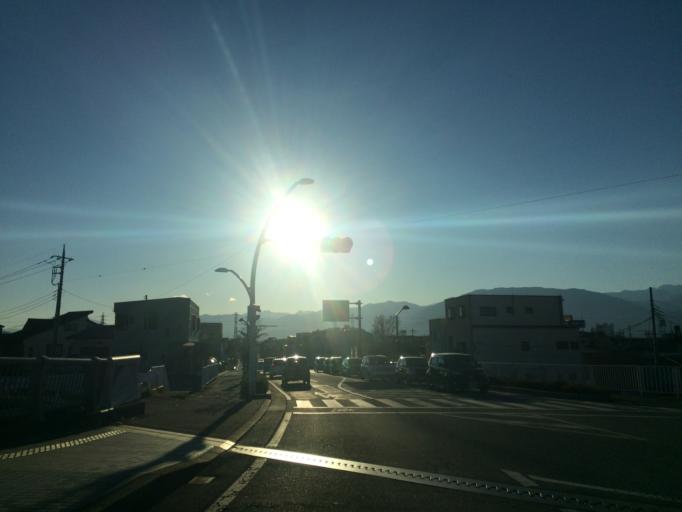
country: JP
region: Yamanashi
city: Kofu-shi
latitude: 35.6480
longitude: 138.5655
